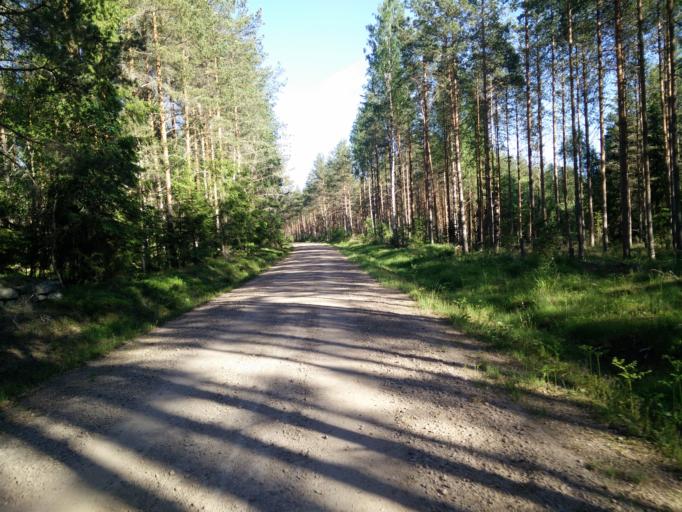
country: SE
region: Vaermland
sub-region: Hagfors Kommun
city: Hagfors
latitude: 60.0147
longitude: 13.5708
